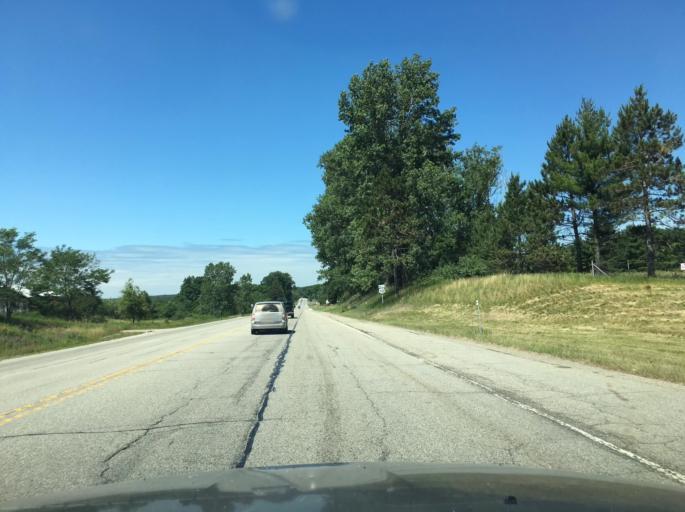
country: US
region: Michigan
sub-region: Osceola County
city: Reed City
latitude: 43.8878
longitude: -85.6224
